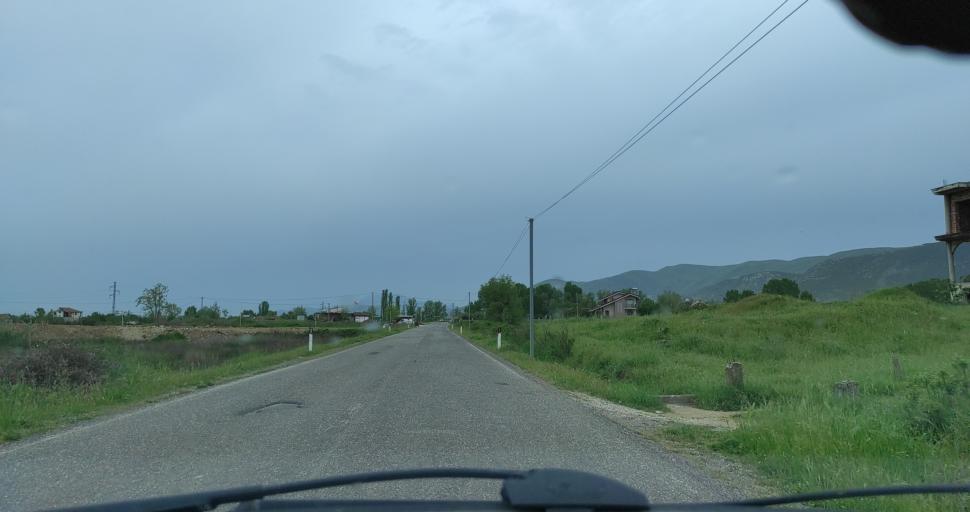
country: AL
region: Lezhe
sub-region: Rrethi i Kurbinit
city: Mamurras
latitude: 41.5967
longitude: 19.6990
